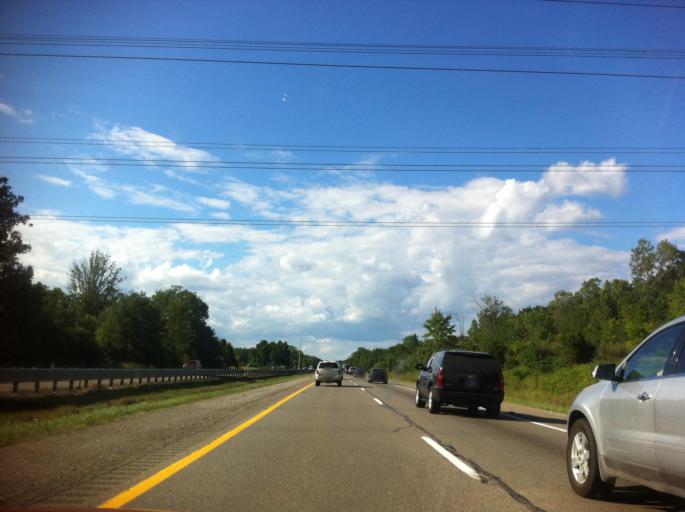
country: US
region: Michigan
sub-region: Washtenaw County
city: Ann Arbor
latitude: 42.3505
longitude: -83.7468
